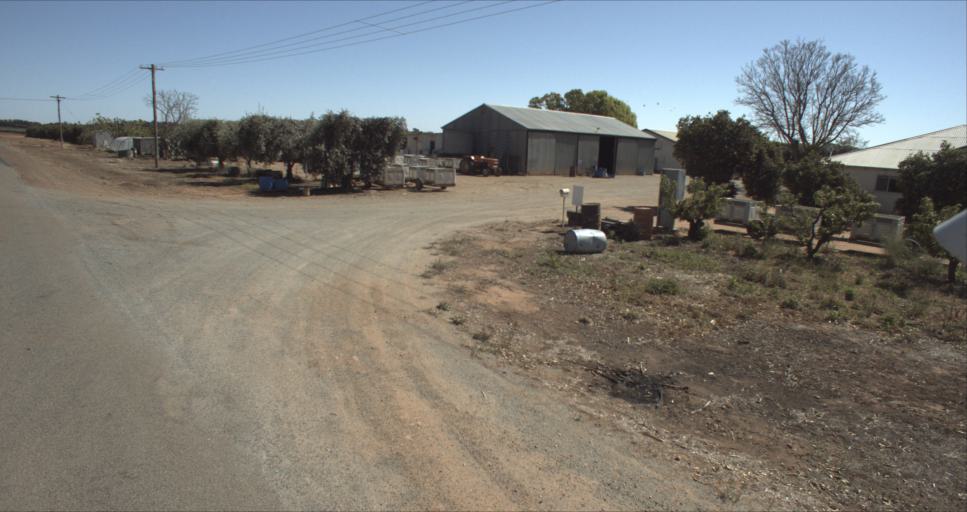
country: AU
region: New South Wales
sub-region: Leeton
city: Leeton
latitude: -34.5376
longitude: 146.3342
